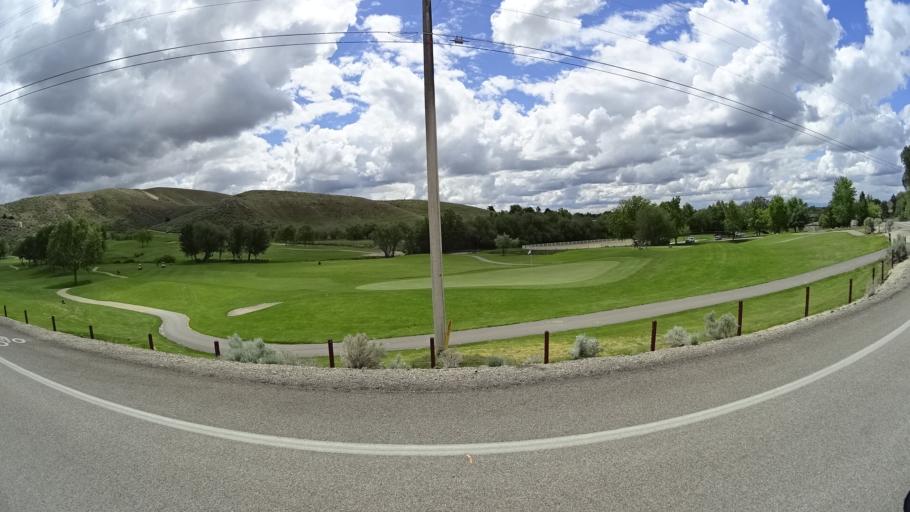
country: US
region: Idaho
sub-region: Ada County
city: Garden City
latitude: 43.6605
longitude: -116.2297
